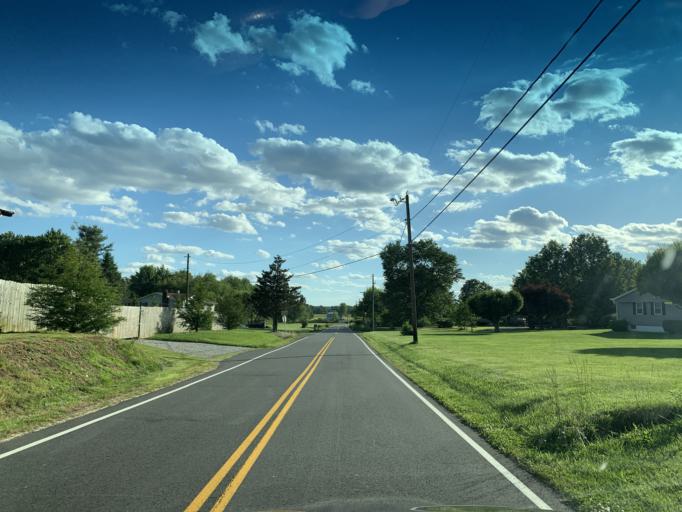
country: US
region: Maryland
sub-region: Cecil County
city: North East
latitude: 39.6752
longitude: -75.9669
